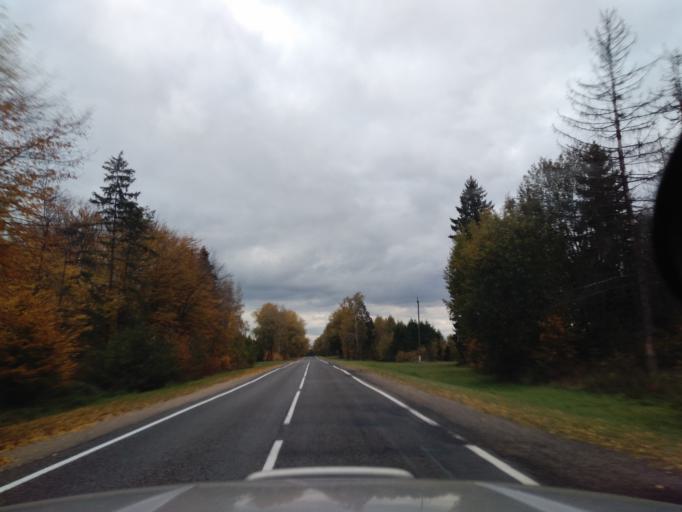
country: BY
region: Minsk
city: Slutsk
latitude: 53.2202
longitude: 27.5161
